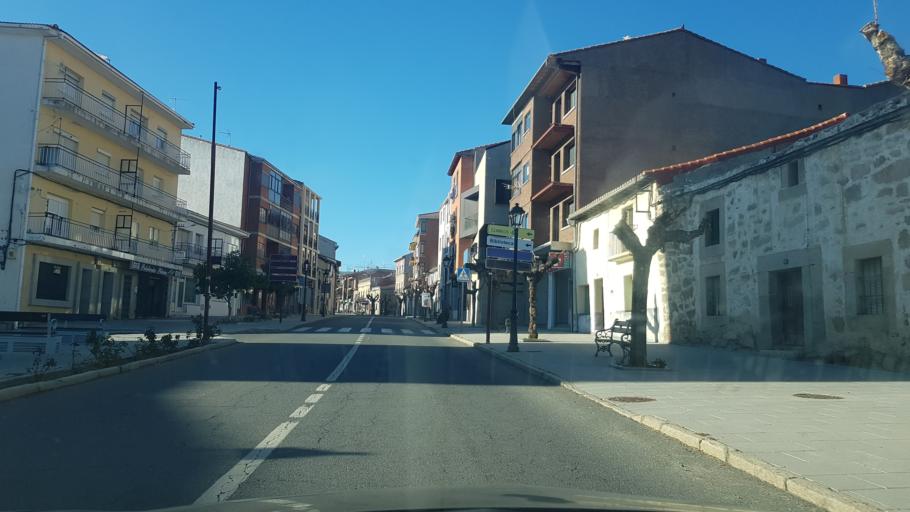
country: ES
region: Castille and Leon
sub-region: Provincia de Avila
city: Barraco
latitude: 40.4762
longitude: -4.6407
